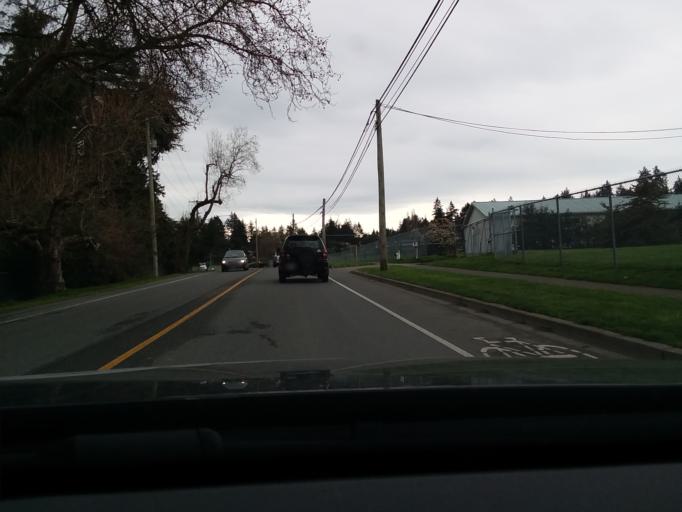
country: CA
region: British Columbia
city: North Saanich
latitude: 48.6227
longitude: -123.4183
